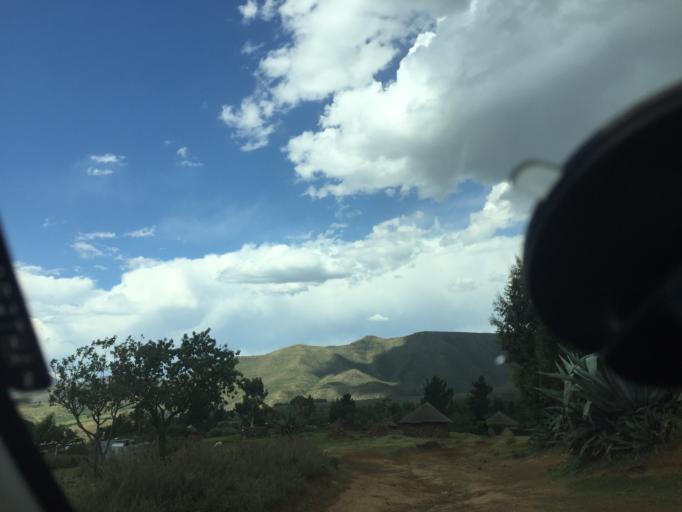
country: LS
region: Maseru
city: Nako
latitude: -29.5914
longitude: 27.7535
